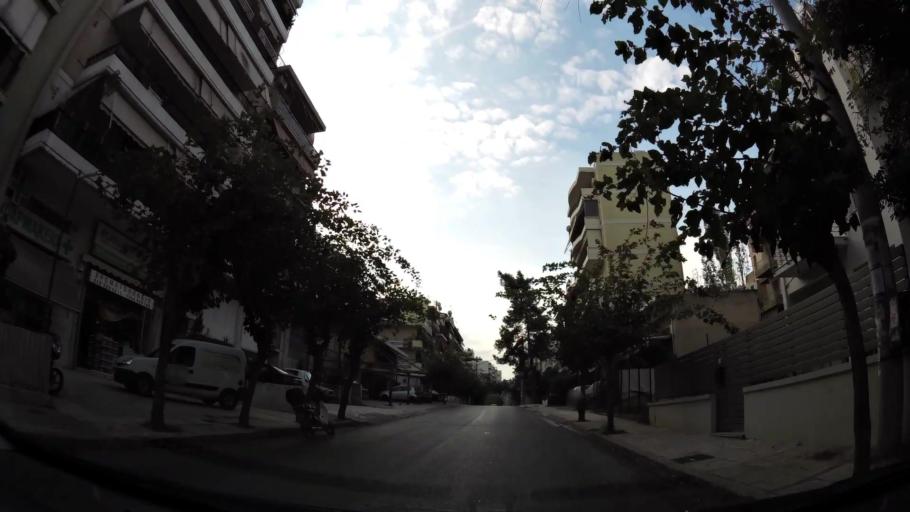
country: GR
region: Attica
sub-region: Nomarchia Athinas
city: Kipseli
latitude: 38.0112
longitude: 23.7390
